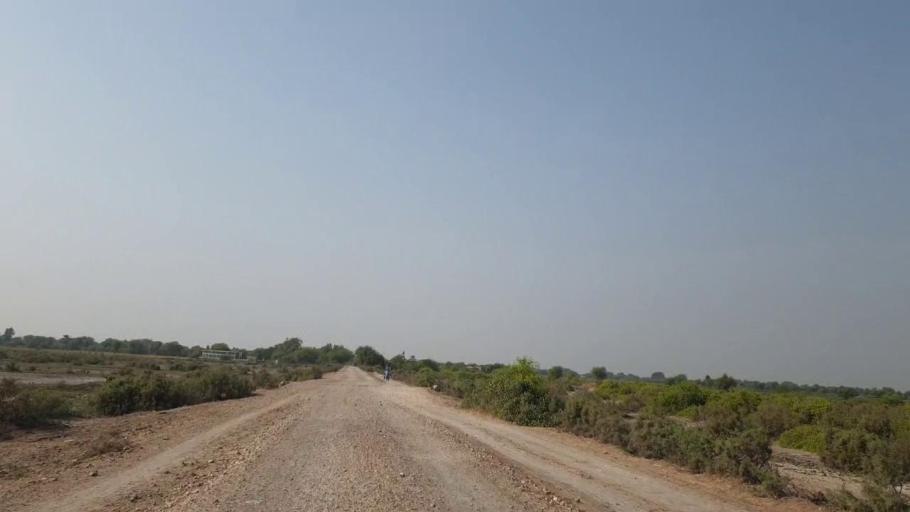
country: PK
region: Sindh
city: Kario
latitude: 24.9405
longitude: 68.5434
